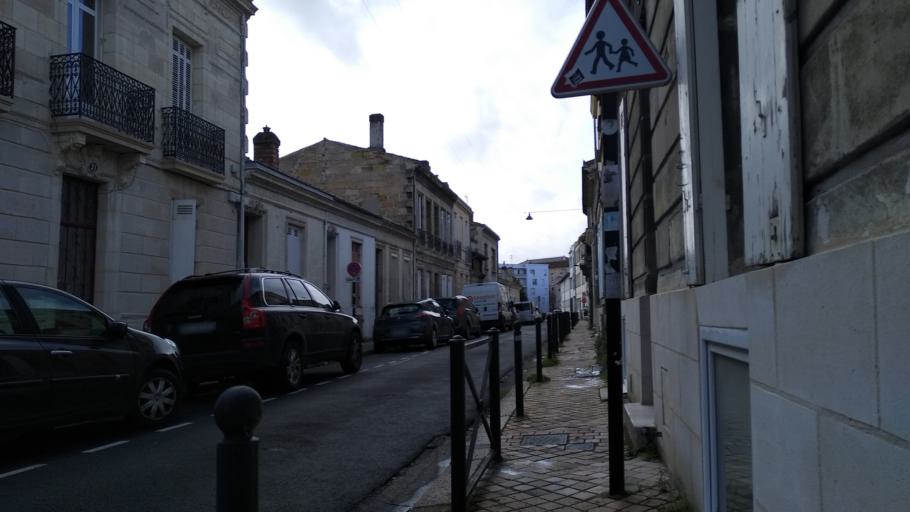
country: FR
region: Aquitaine
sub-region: Departement de la Gironde
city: Bordeaux
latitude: 44.8253
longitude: -0.5741
